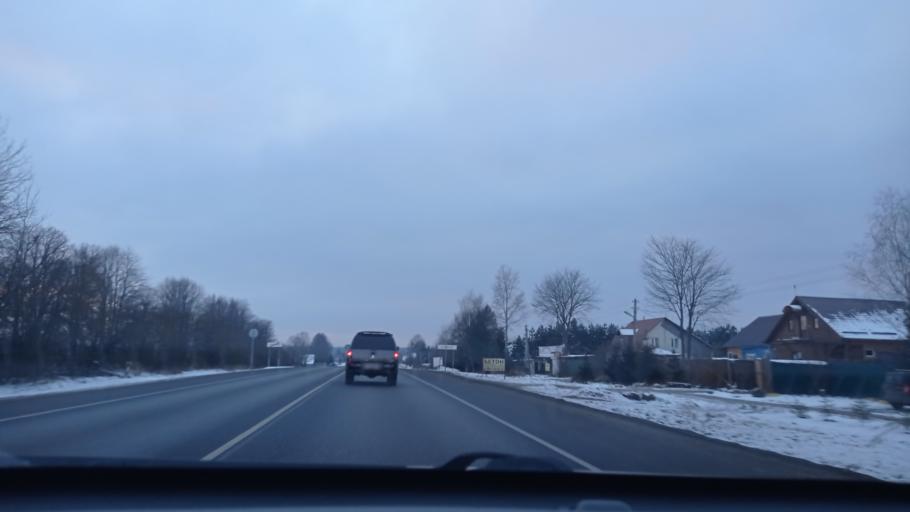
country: RU
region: Moskovskaya
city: Ateptsevo
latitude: 55.2034
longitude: 36.9306
